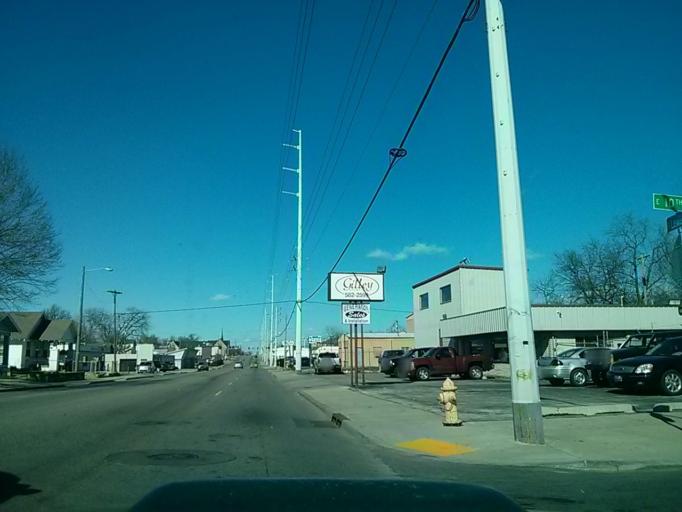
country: US
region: Oklahoma
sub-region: Tulsa County
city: Tulsa
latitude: 36.1488
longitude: -95.9581
